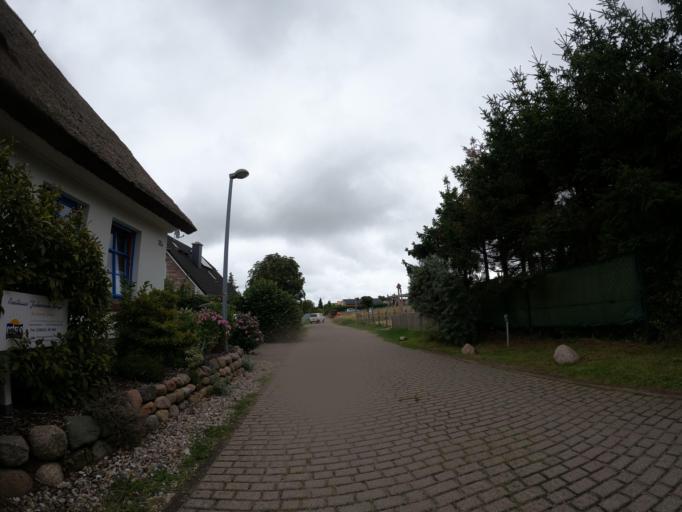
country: DE
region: Mecklenburg-Vorpommern
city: Ostseebad Gohren
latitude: 54.3072
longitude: 13.6827
